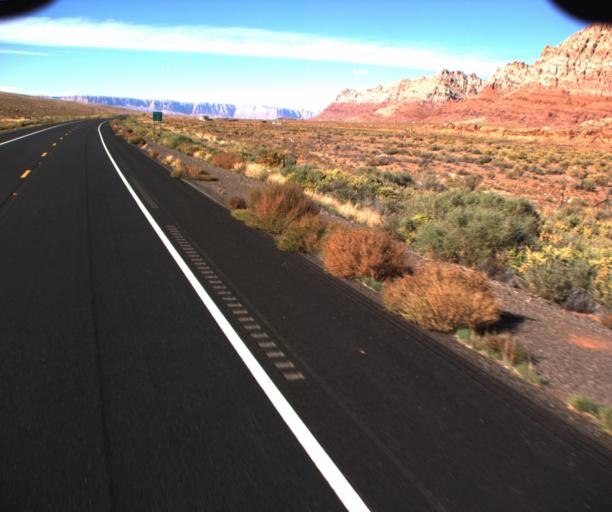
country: US
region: Arizona
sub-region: Coconino County
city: LeChee
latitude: 36.5418
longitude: -111.6179
